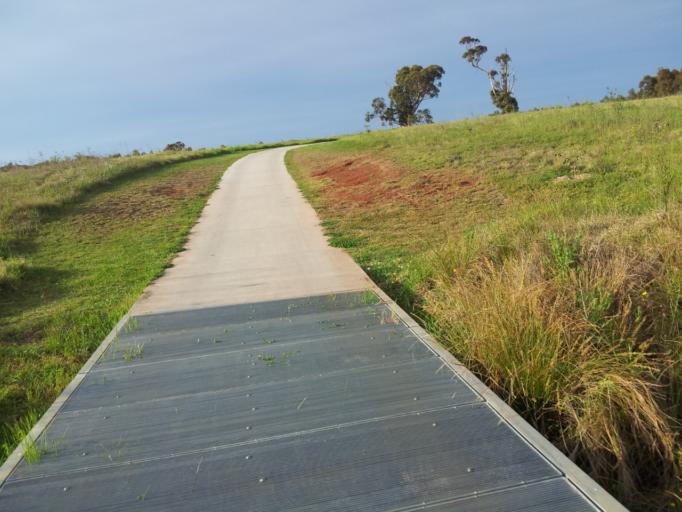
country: AU
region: New South Wales
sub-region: Fairfield
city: Horsley Park
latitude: -33.8593
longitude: 150.8699
